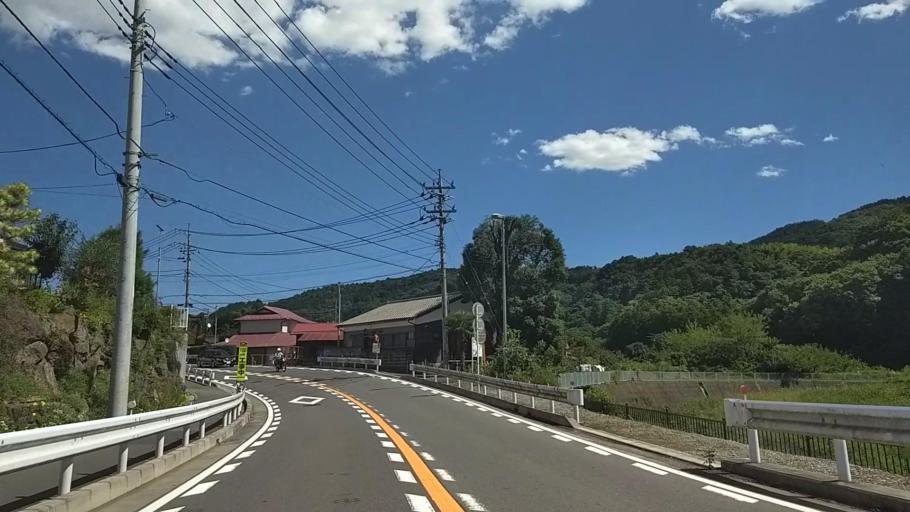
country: JP
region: Tokyo
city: Hachioji
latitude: 35.5664
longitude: 139.2658
